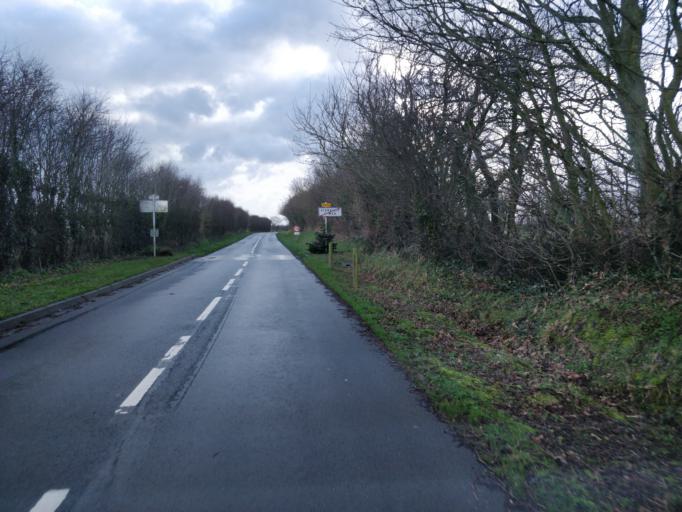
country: FR
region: Lower Normandy
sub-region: Departement du Calvados
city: Le Molay-Littry
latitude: 49.3712
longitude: -0.8988
